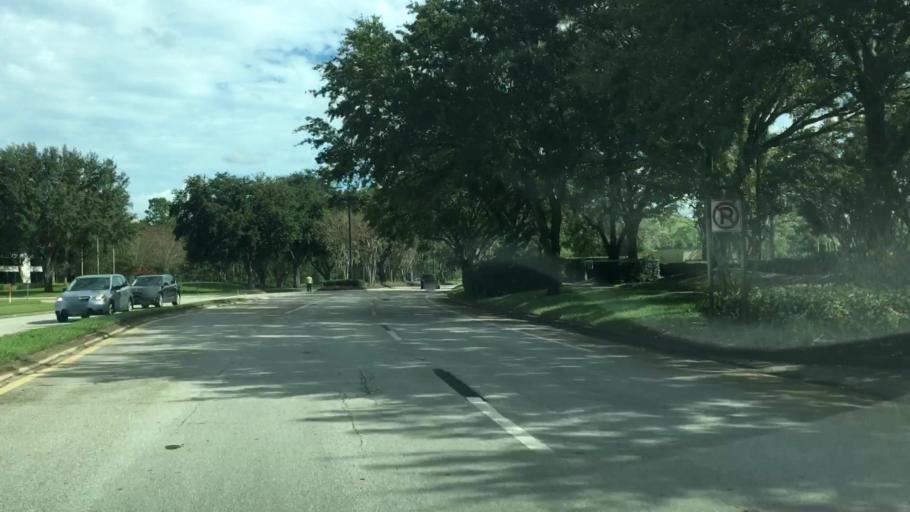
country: US
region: Florida
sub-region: Orange County
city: Conway
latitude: 28.4622
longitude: -81.3046
